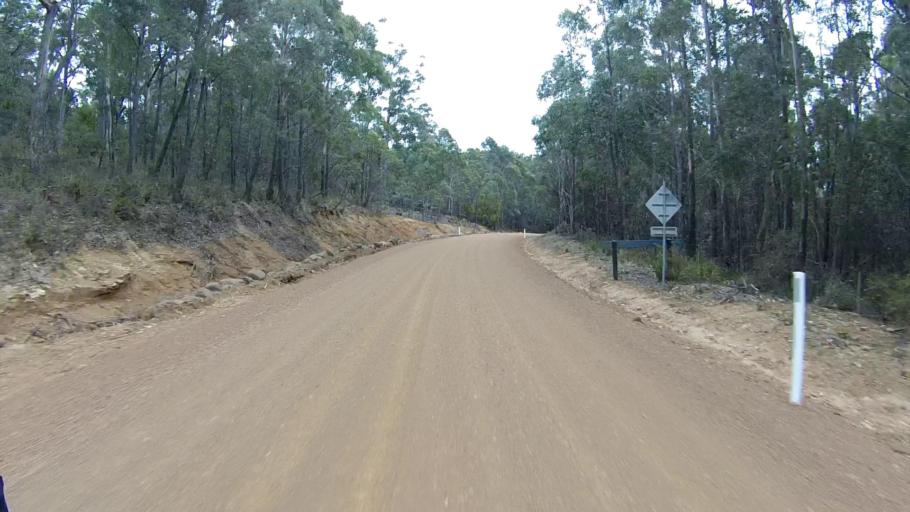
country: AU
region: Tasmania
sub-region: Sorell
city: Sorell
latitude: -42.5983
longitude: 147.8851
